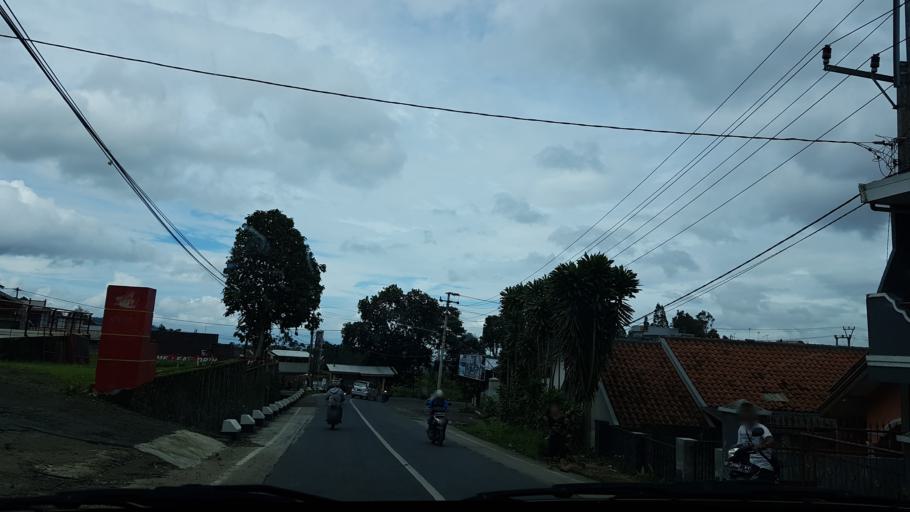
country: ID
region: West Java
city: Banjar
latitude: -7.1125
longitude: 107.4405
